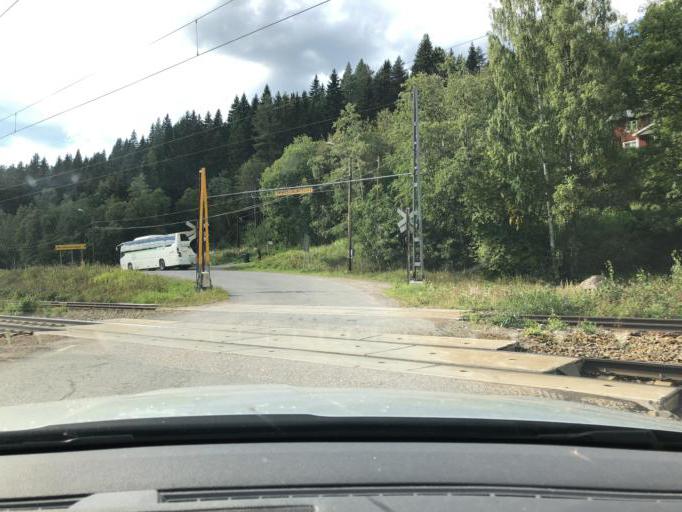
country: SE
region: Vaesternorrland
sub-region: Solleftea Kommun
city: Solleftea
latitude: 63.2115
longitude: 17.1867
